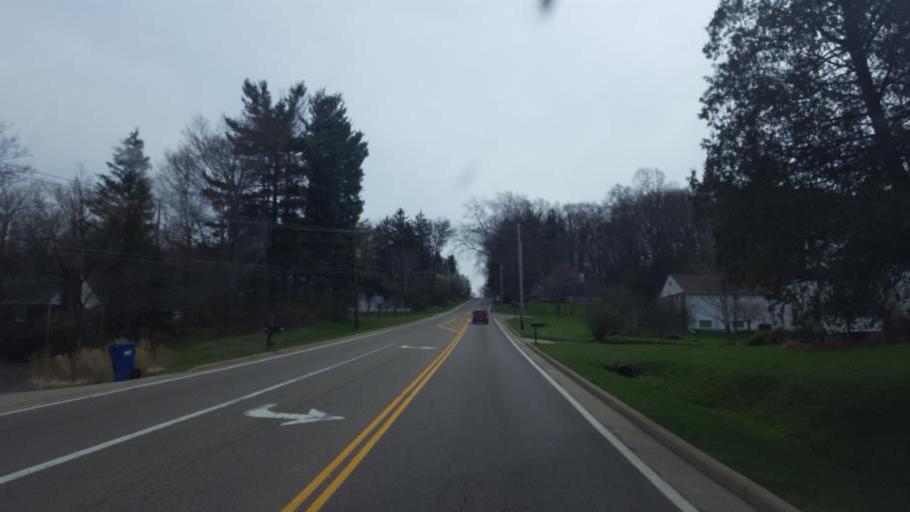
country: US
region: Ohio
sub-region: Knox County
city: Mount Vernon
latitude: 40.3881
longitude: -82.4634
